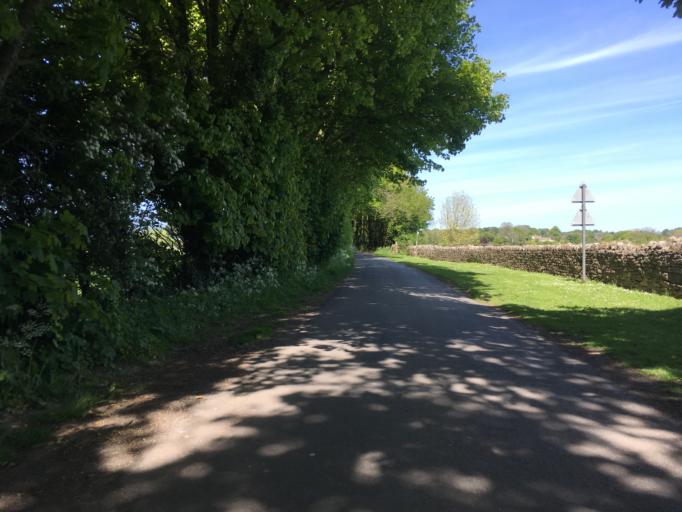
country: GB
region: England
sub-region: Gloucestershire
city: Brimscombe
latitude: 51.7338
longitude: -2.1843
